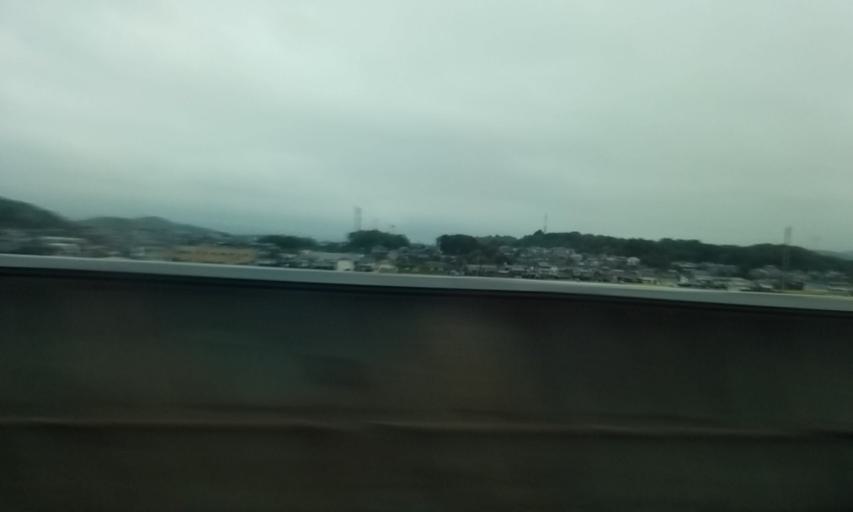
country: JP
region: Okayama
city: Soja
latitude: 34.6499
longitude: 133.8264
